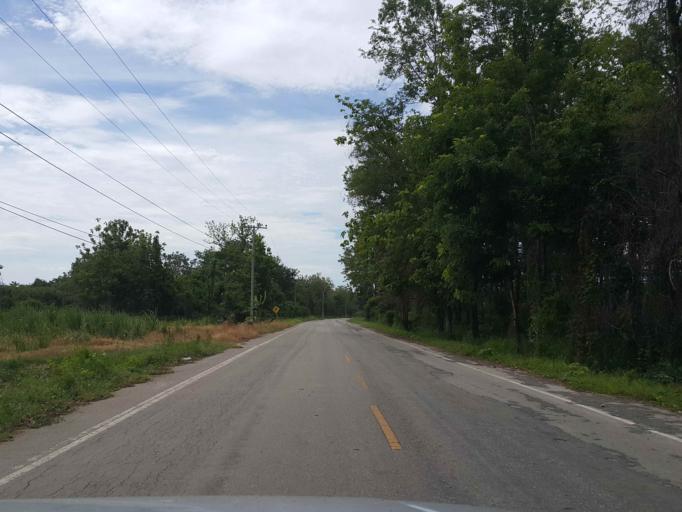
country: TH
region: Sukhothai
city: Ban Dan Lan Hoi
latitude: 17.0834
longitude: 99.4784
